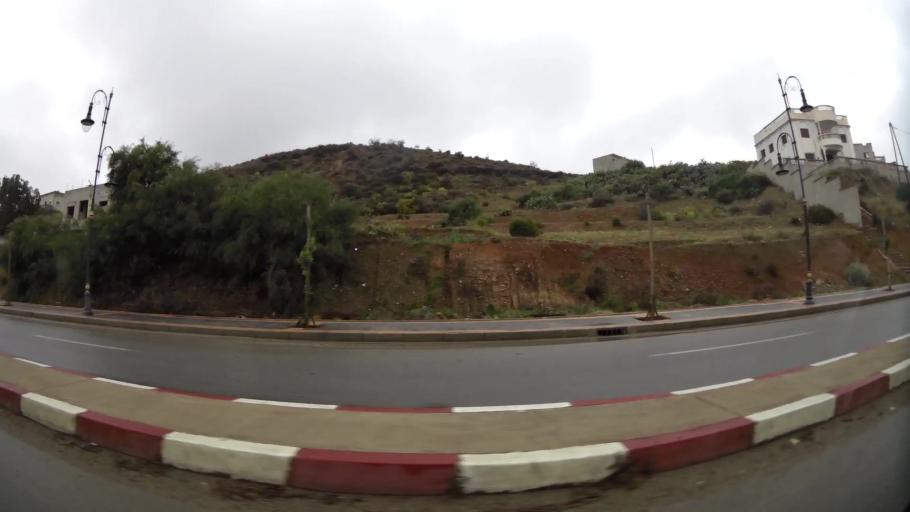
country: MA
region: Taza-Al Hoceima-Taounate
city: Imzourene
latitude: 35.1769
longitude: -3.8785
